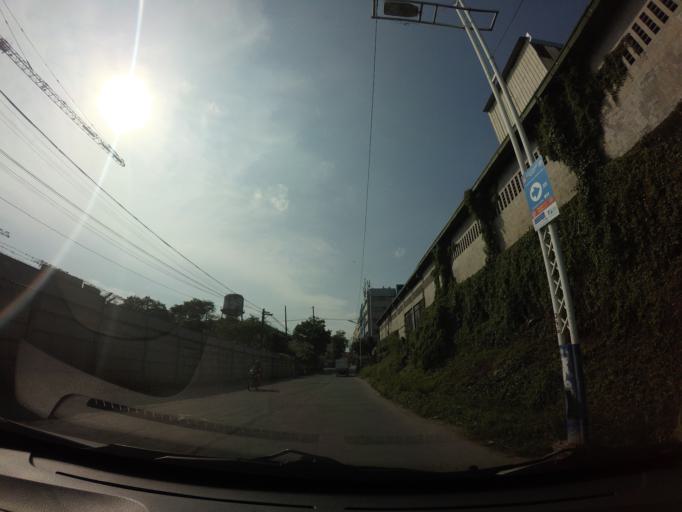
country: PH
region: Metro Manila
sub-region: Makati City
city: Makati City
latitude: 14.5076
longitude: 121.0390
